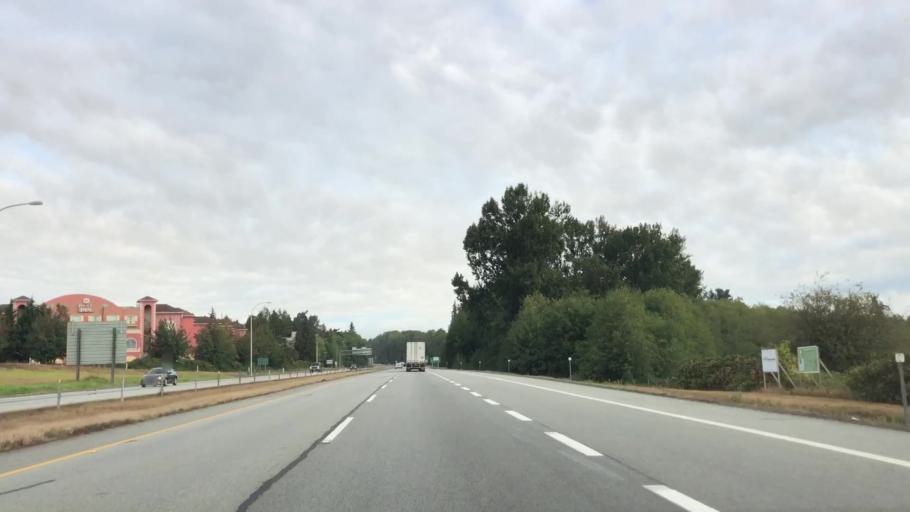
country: US
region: Washington
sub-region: Whatcom County
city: Blaine
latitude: 49.0212
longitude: -122.7620
